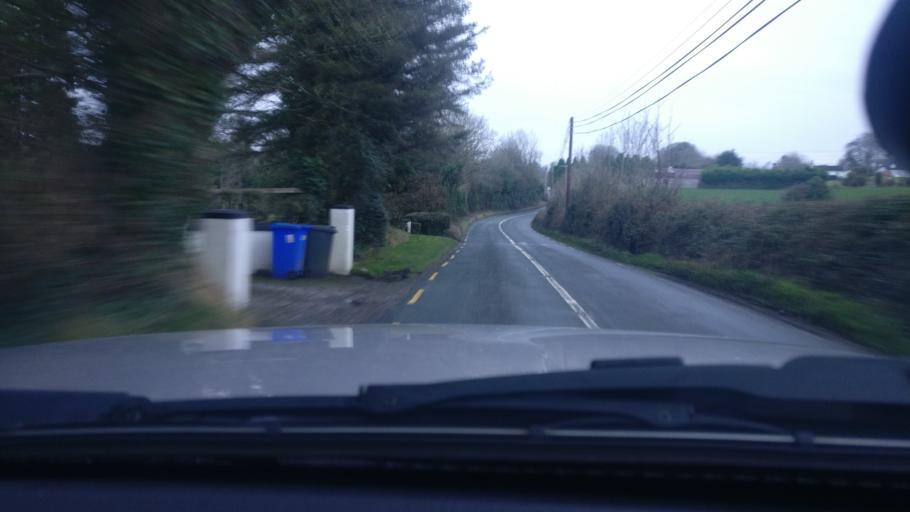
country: IE
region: Connaught
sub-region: County Galway
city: Loughrea
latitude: 53.1658
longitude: -8.5211
